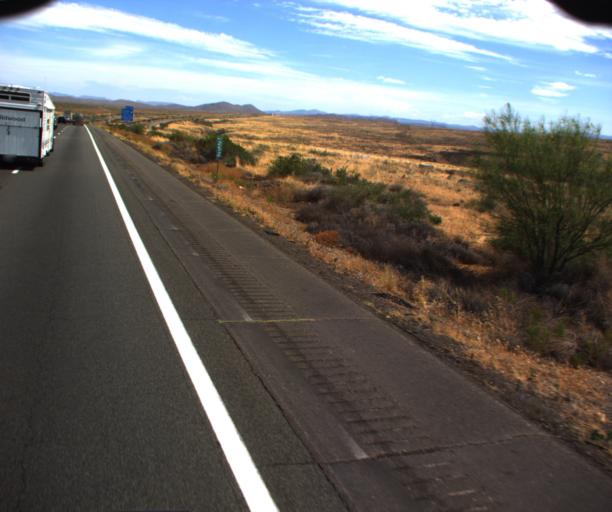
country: US
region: Arizona
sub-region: Yavapai County
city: Black Canyon City
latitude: 34.1859
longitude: -112.1331
